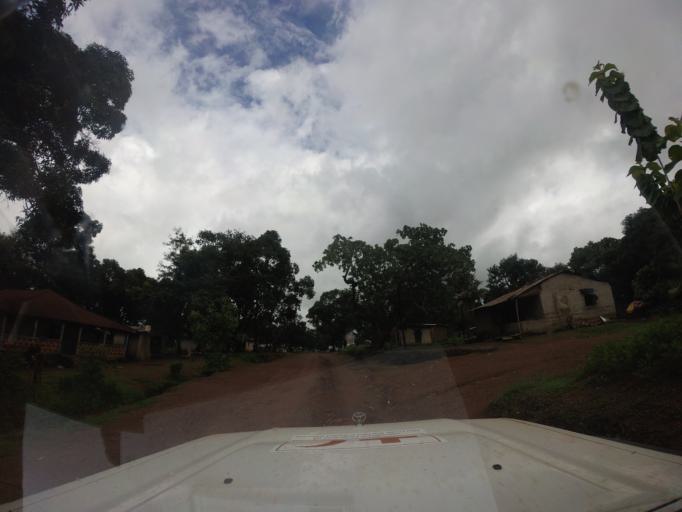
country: SL
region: Northern Province
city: Kukuna
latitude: 9.2855
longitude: -12.6721
